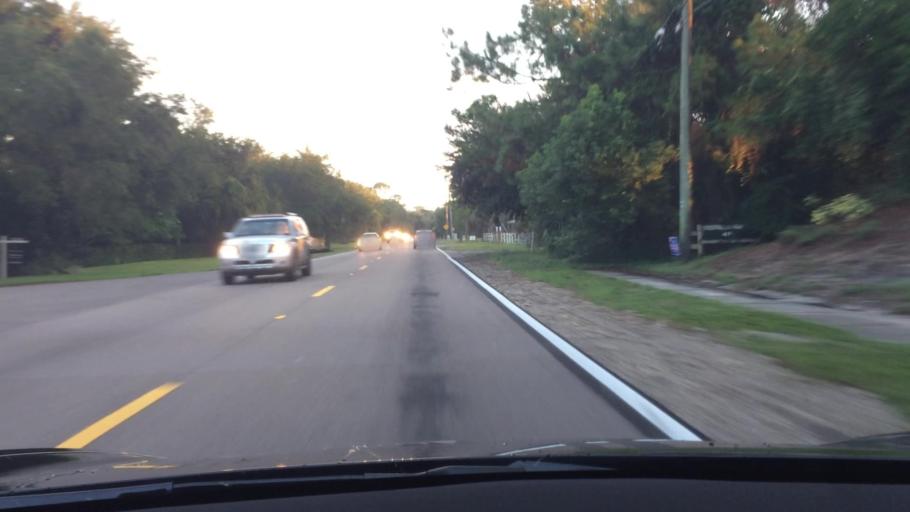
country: US
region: Florida
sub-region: Hillsborough County
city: Citrus Park
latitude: 28.1197
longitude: -82.5787
